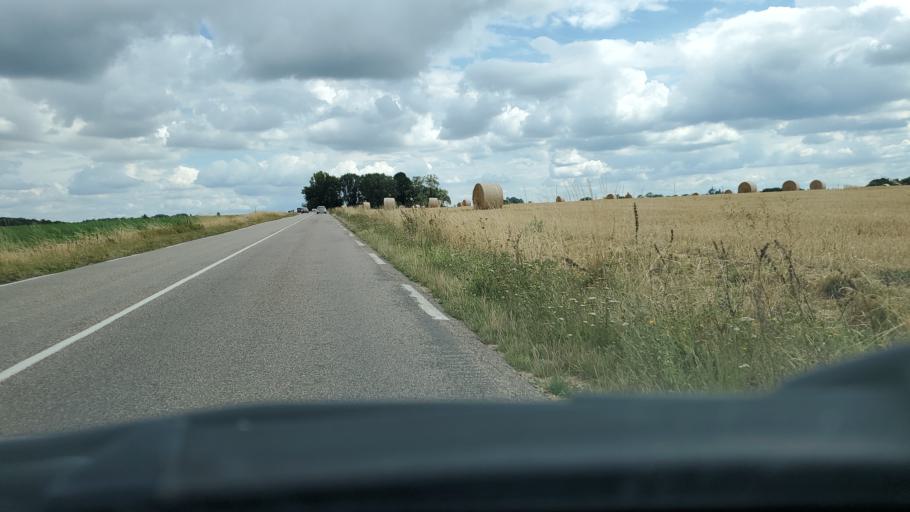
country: FR
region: Ile-de-France
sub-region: Departement de Seine-et-Marne
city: Fublaines
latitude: 48.9093
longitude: 2.9249
